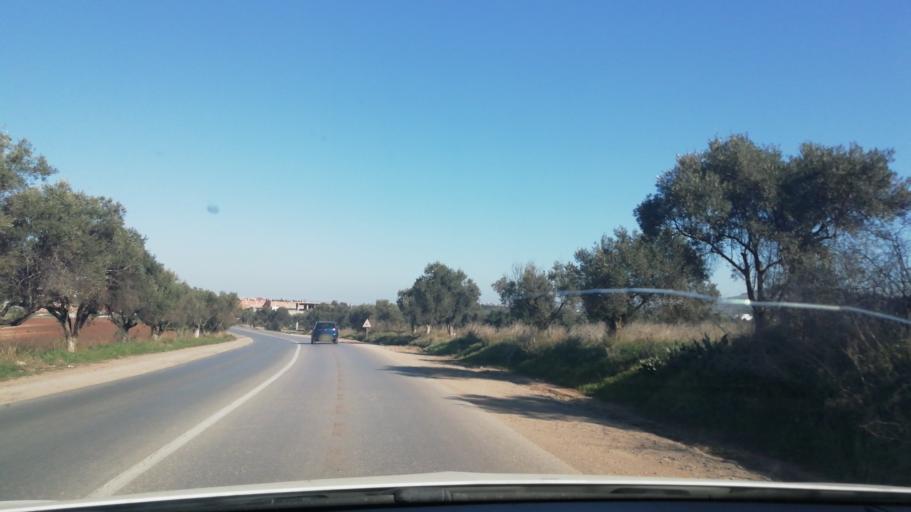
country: DZ
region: Tlemcen
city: Nedroma
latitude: 35.0220
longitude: -1.8919
